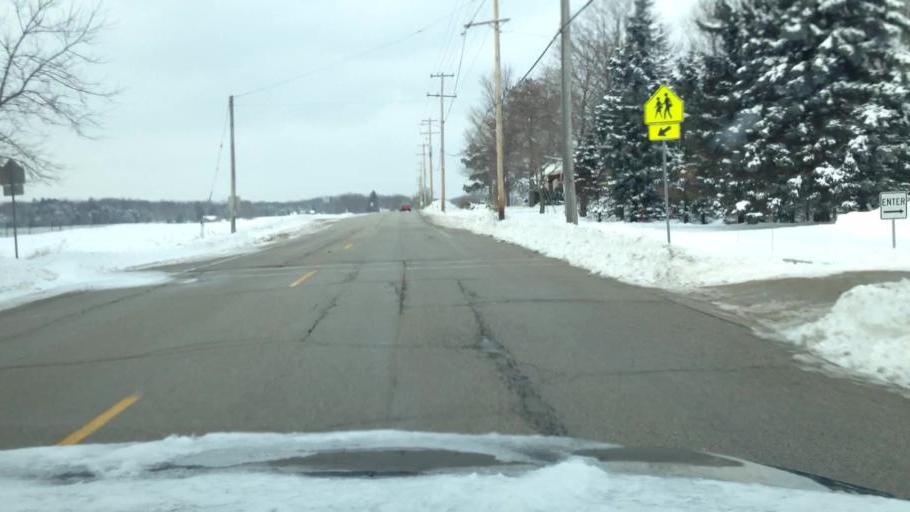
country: US
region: Wisconsin
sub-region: Waukesha County
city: North Prairie
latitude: 42.9379
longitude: -88.4055
